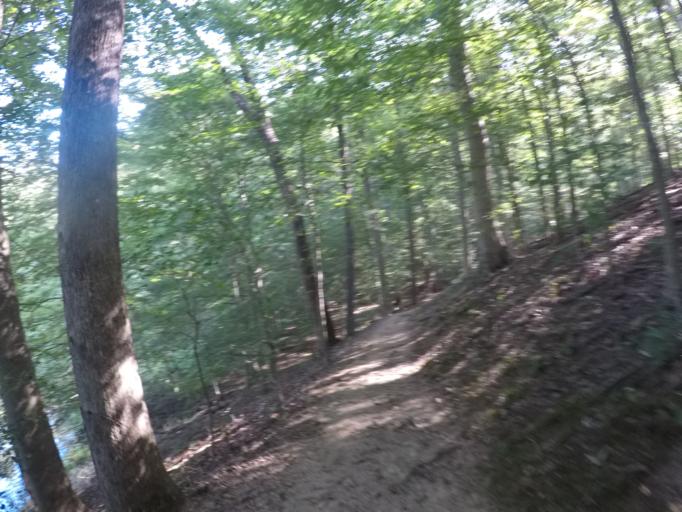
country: US
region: Ohio
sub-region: Lawrence County
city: Ironton
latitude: 38.6081
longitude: -82.6255
